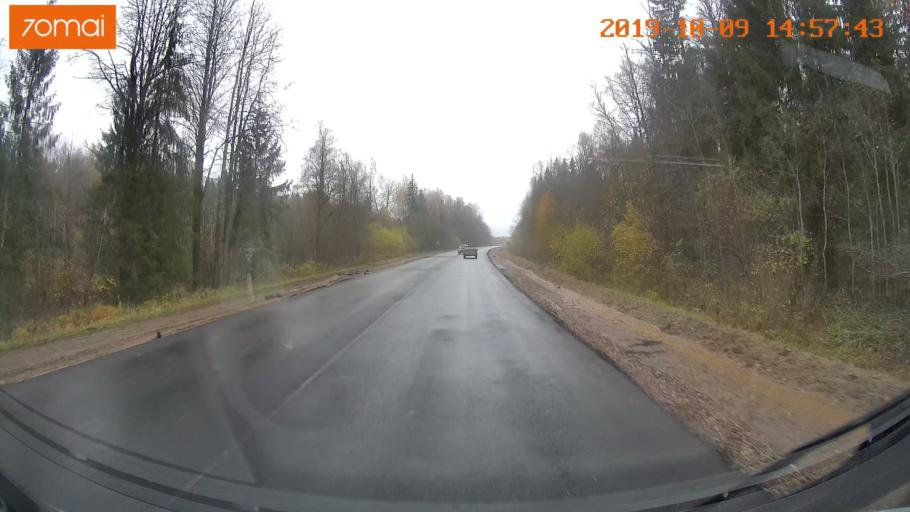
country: RU
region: Kostroma
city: Chistyye Bory
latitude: 58.3348
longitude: 41.6522
